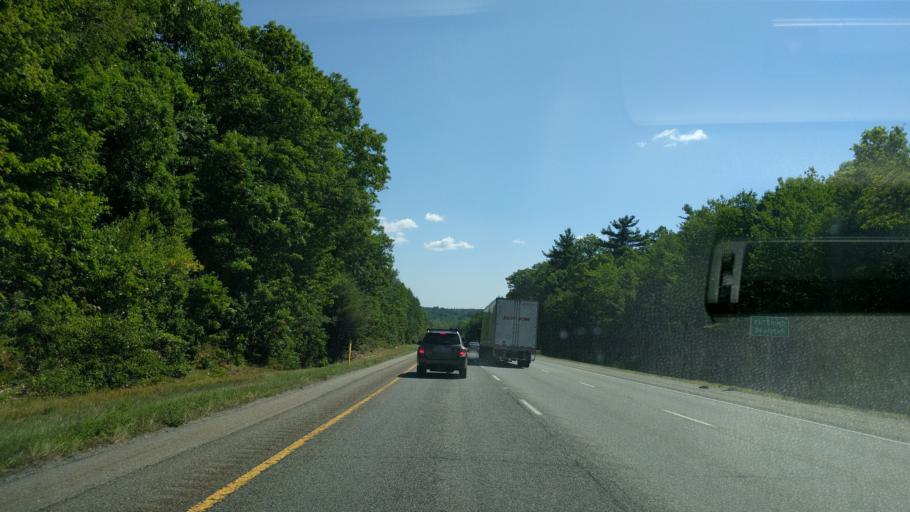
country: US
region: Massachusetts
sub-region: Worcester County
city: Shrewsbury
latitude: 42.3275
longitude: -71.6980
